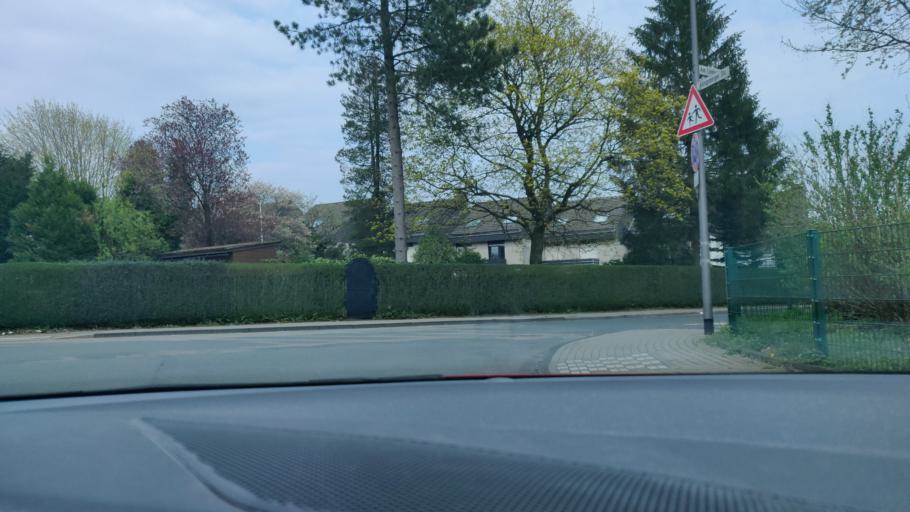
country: DE
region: North Rhine-Westphalia
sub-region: Regierungsbezirk Dusseldorf
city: Velbert
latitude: 51.3300
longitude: 7.0327
